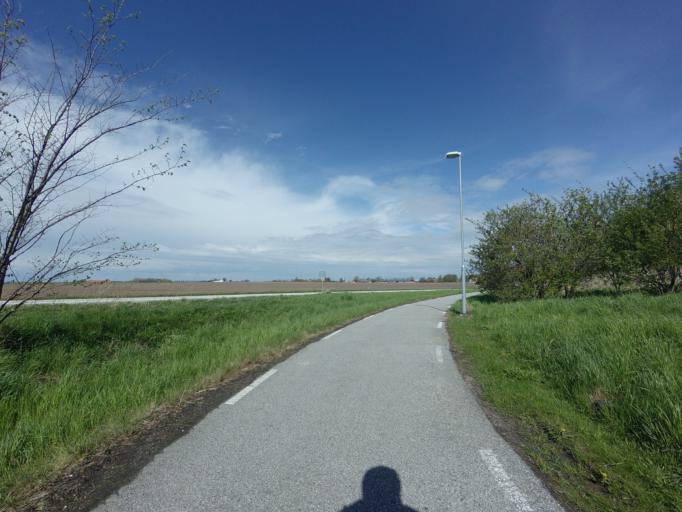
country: SE
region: Skane
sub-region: Malmo
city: Tygelsjo
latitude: 55.4958
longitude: 13.0009
